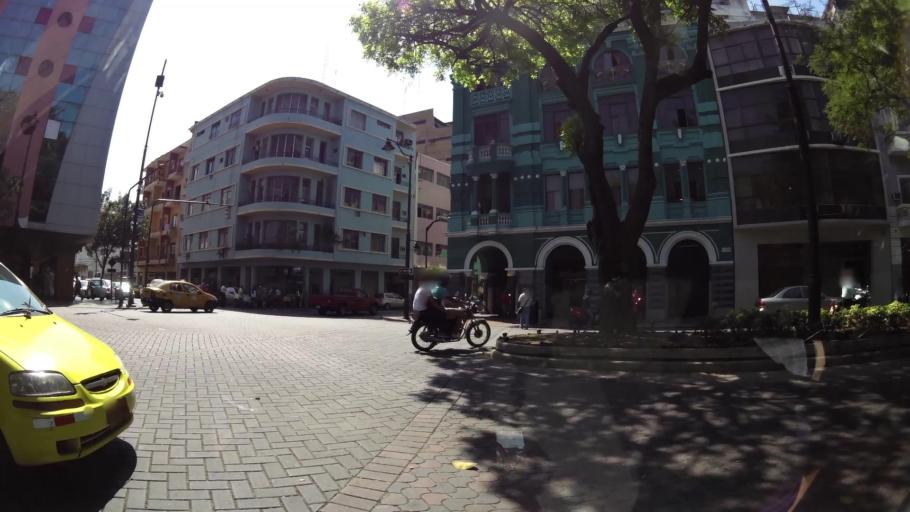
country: EC
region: Guayas
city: Guayaquil
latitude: -2.1894
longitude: -79.8869
